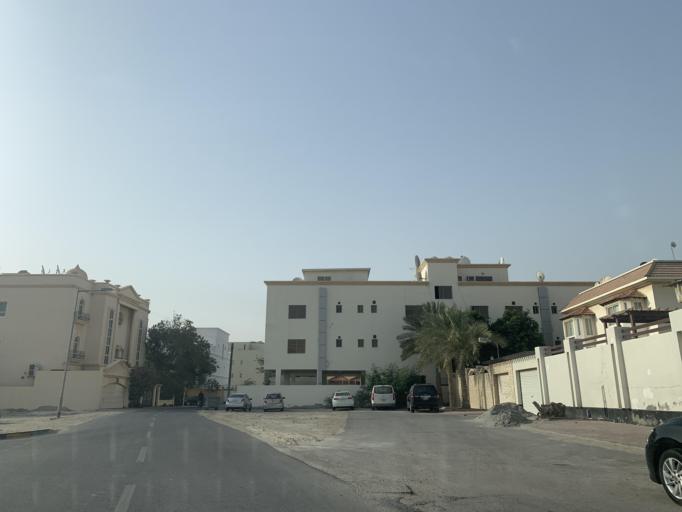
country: BH
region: Northern
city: Madinat `Isa
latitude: 26.1935
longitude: 50.5644
